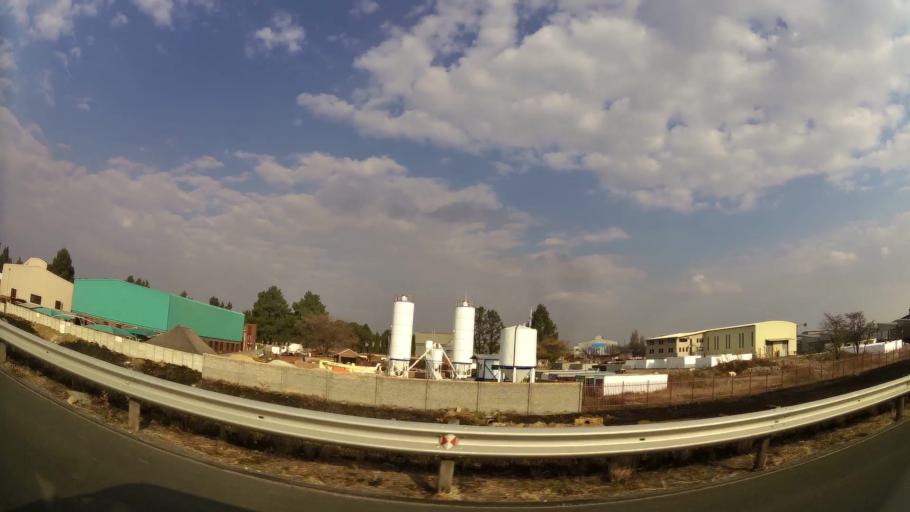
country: ZA
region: Gauteng
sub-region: Ekurhuleni Metropolitan Municipality
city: Springs
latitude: -26.2774
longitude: 28.4581
